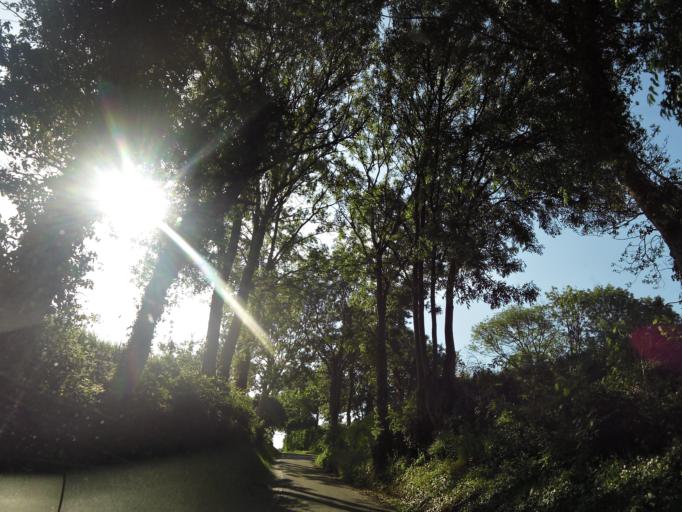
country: NL
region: Limburg
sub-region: Gemeente Voerendaal
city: Ubachsberg
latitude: 50.8434
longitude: 5.9156
